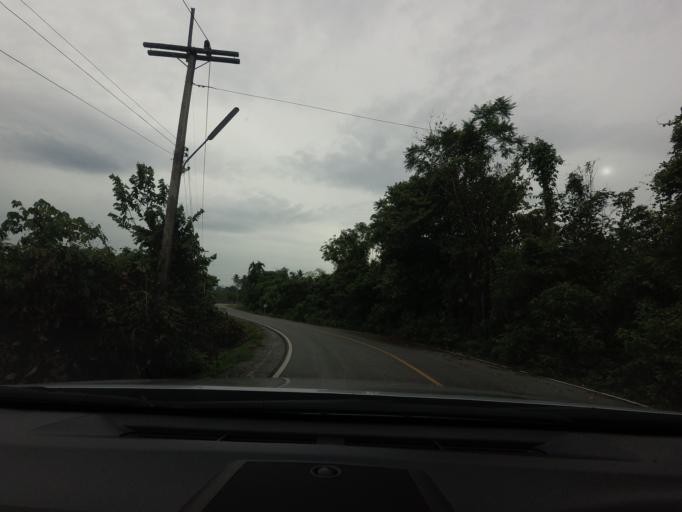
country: TH
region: Narathiwat
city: Rueso
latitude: 6.4145
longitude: 101.5209
